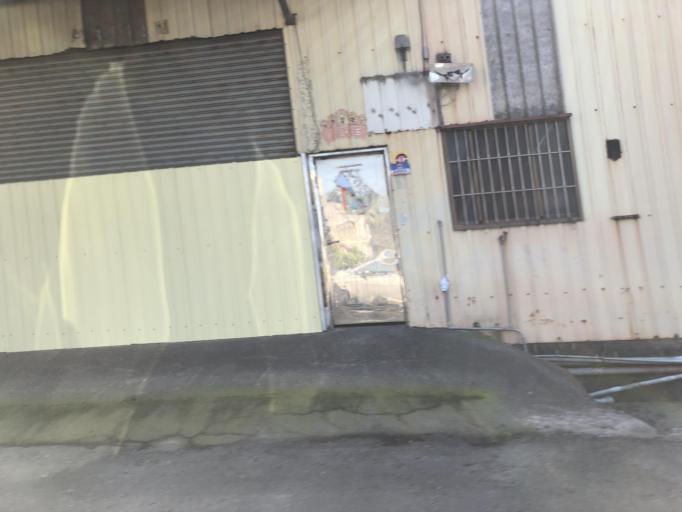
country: TW
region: Taiwan
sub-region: Tainan
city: Tainan
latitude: 23.0321
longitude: 120.2971
